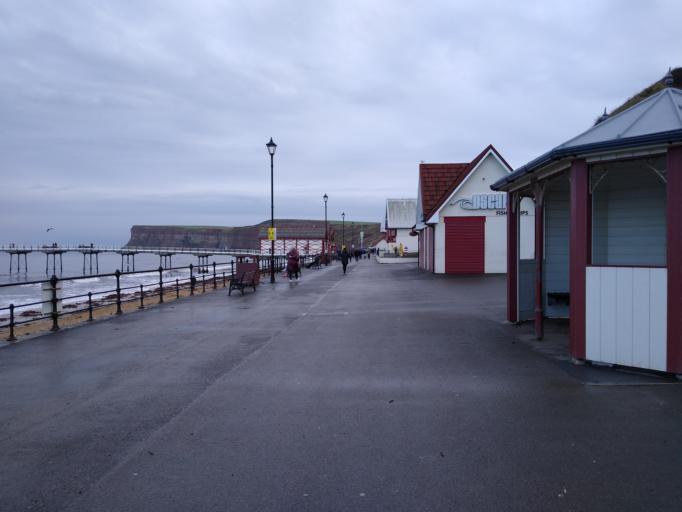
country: GB
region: England
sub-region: Redcar and Cleveland
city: Saltburn-by-the-Sea
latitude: 54.5866
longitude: -0.9725
